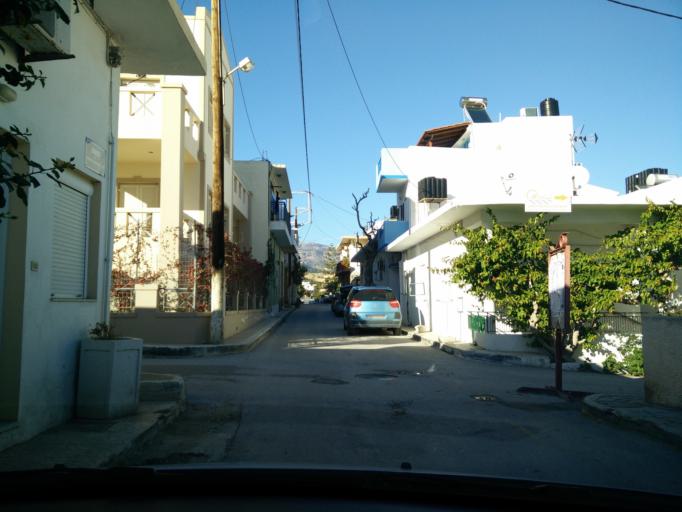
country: GR
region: Crete
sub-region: Nomos Lasithiou
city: Gra Liyia
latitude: 35.0043
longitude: 25.5843
